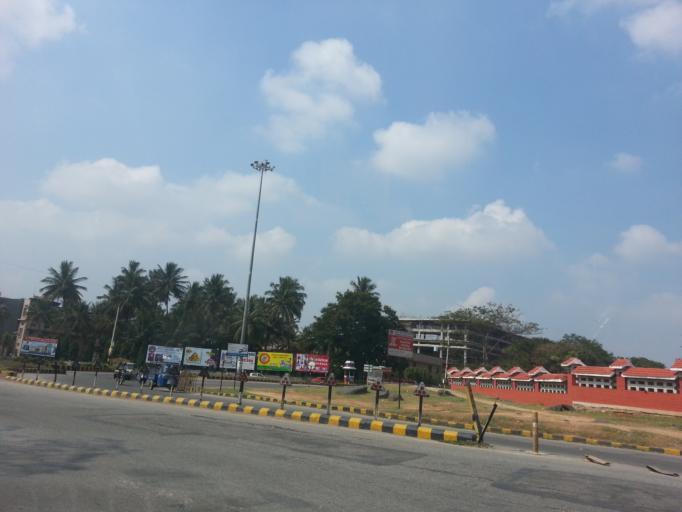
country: IN
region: Karnataka
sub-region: Mysore
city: Mysore
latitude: 12.3330
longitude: 76.6564
